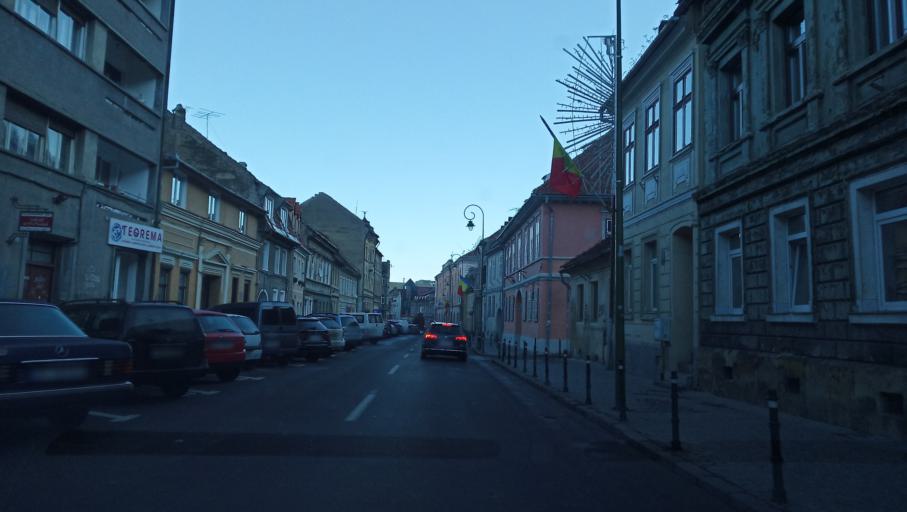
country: RO
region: Brasov
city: Brasov
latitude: 45.6421
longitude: 25.5937
